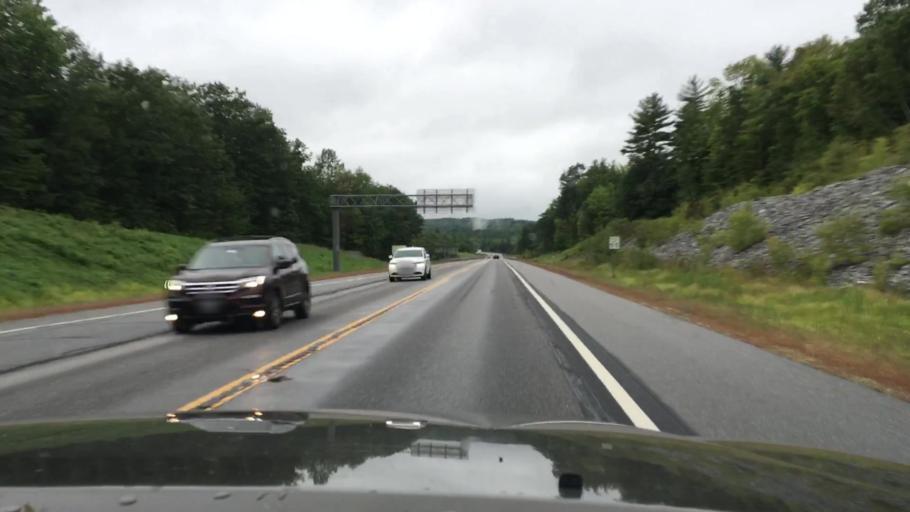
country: US
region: New Hampshire
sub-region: Hillsborough County
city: Hillsborough
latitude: 43.1168
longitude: -71.9248
